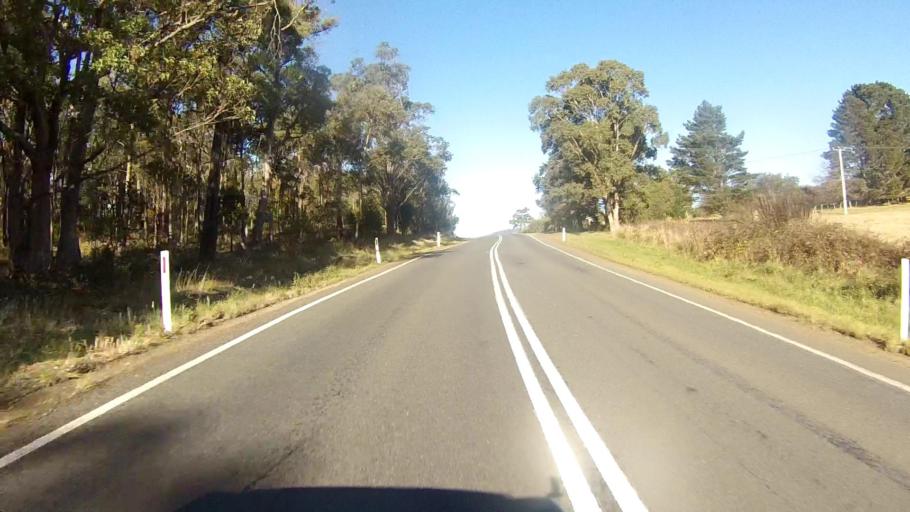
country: AU
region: Tasmania
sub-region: Sorell
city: Sorell
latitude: -42.8245
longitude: 147.8057
